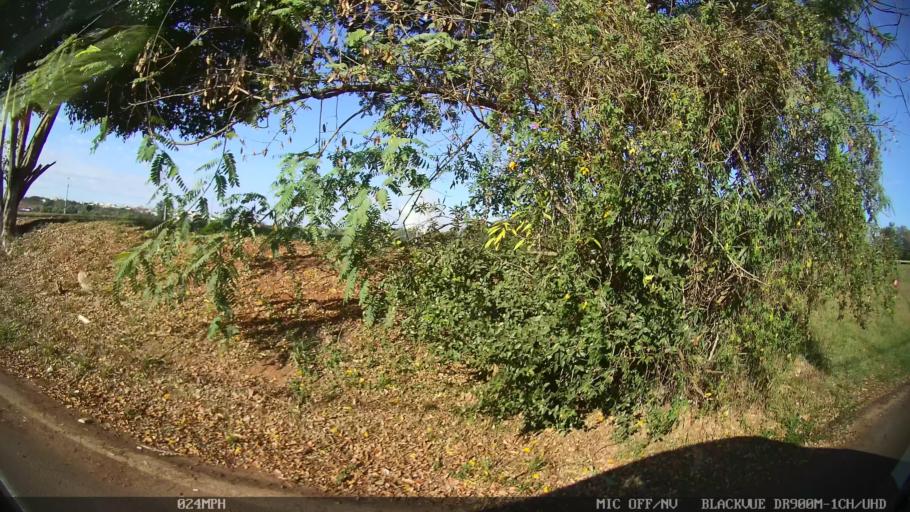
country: BR
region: Sao Paulo
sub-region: Piracicaba
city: Piracicaba
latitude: -22.6917
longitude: -47.6350
